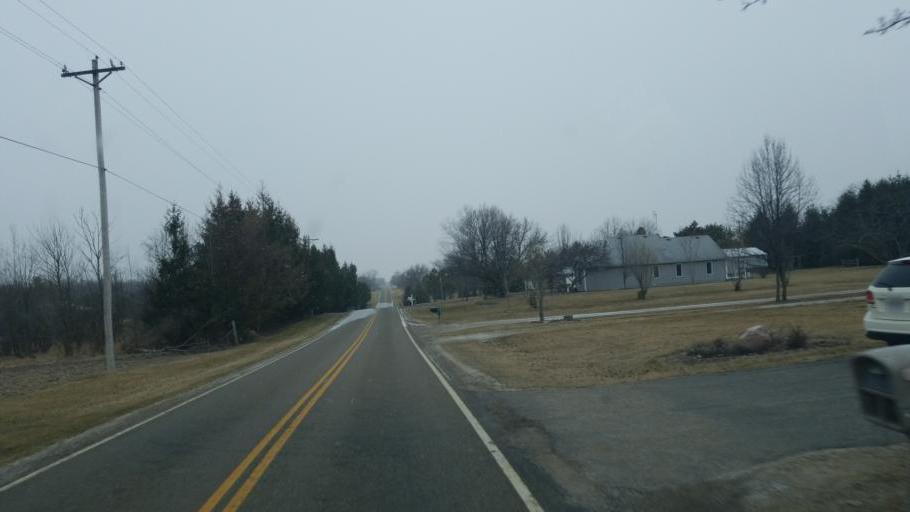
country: US
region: Ohio
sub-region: Defiance County
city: Hicksville
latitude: 41.3250
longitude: -84.7721
